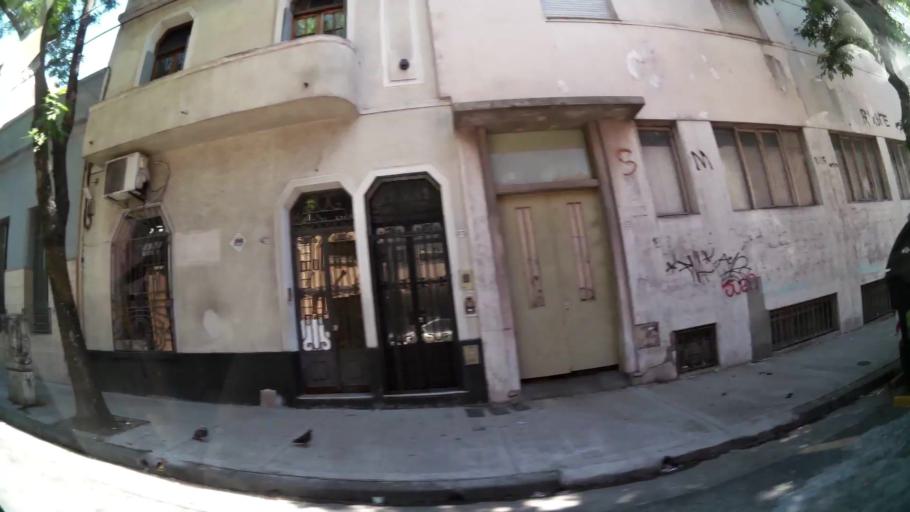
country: AR
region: Buenos Aires F.D.
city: Buenos Aires
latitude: -34.6309
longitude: -58.3838
